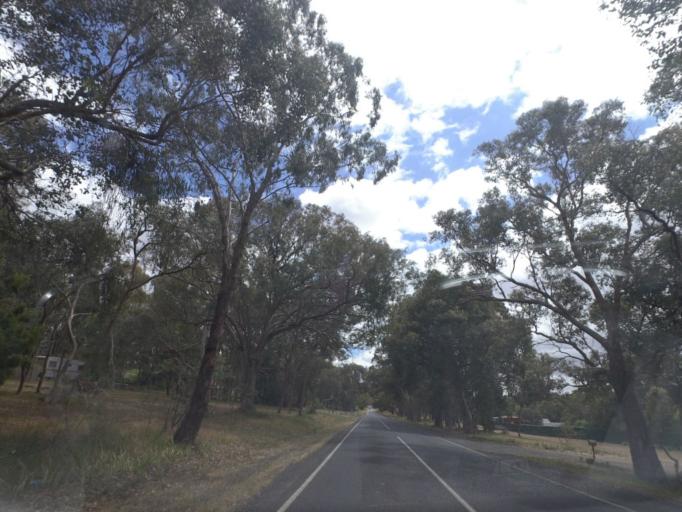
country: AU
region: Victoria
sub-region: Whittlesea
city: Whittlesea
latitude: -37.2262
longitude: 145.0493
